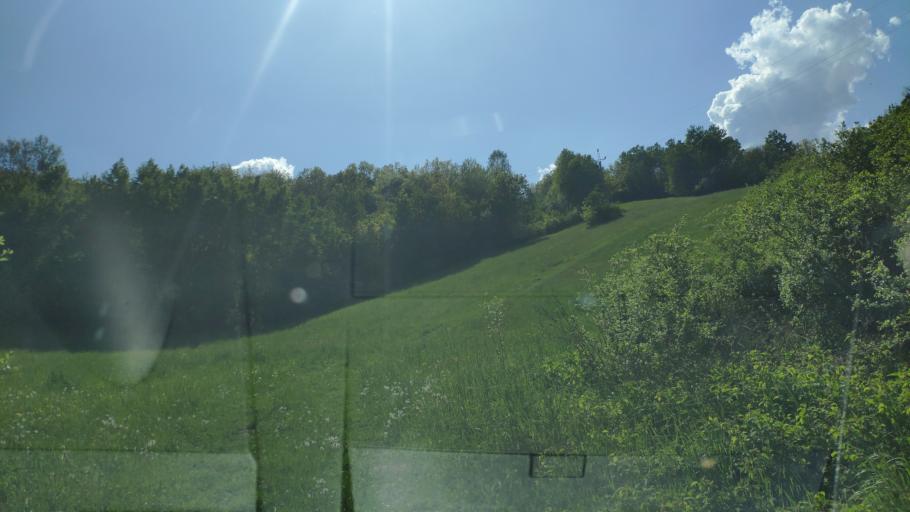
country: SK
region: Presovsky
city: Sabinov
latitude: 49.0498
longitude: 21.1565
